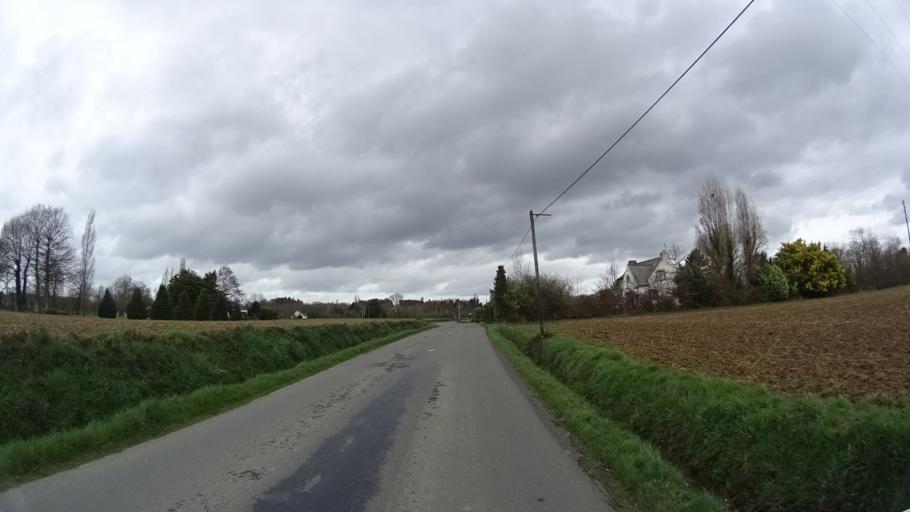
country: FR
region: Brittany
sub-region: Departement d'Ille-et-Vilaine
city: Saint-Gilles
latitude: 48.1667
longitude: -1.8301
